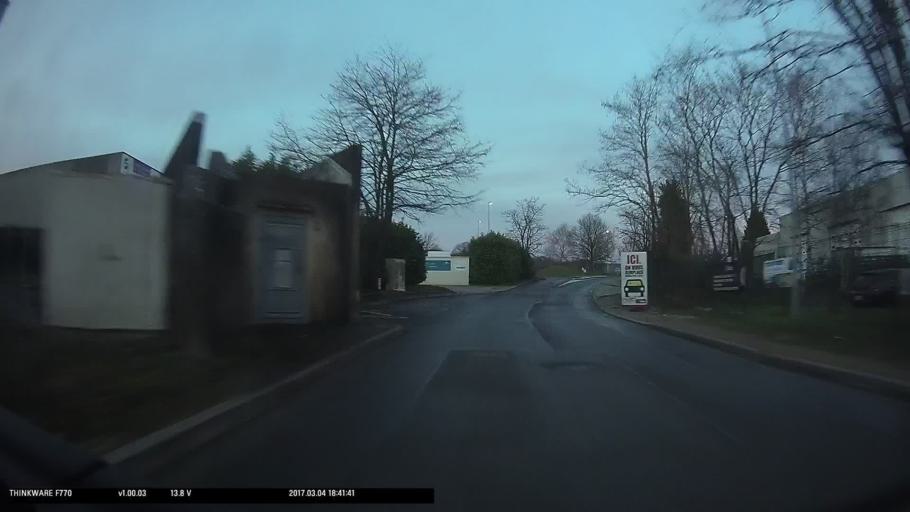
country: FR
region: Ile-de-France
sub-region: Departement du Val-d'Oise
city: Marines
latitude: 49.1480
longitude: 1.9683
